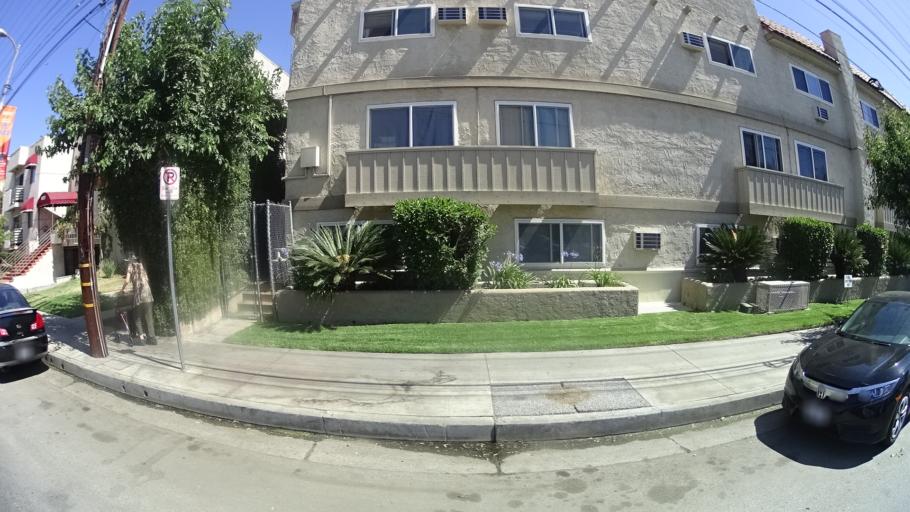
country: US
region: California
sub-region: Los Angeles County
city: Van Nuys
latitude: 34.1939
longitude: -118.4930
